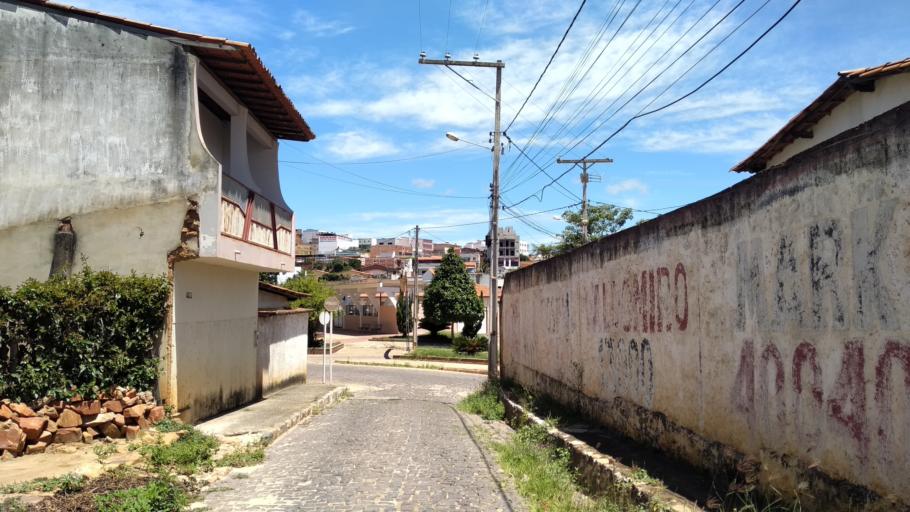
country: BR
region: Bahia
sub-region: Caetite
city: Caetite
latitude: -14.0697
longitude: -42.4815
